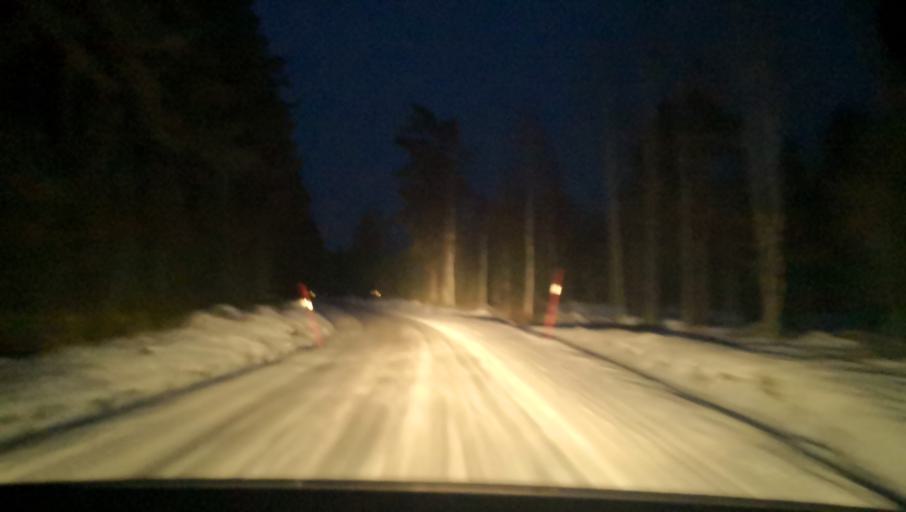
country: SE
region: Uppsala
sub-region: Heby Kommun
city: Tarnsjo
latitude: 60.2773
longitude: 16.8009
